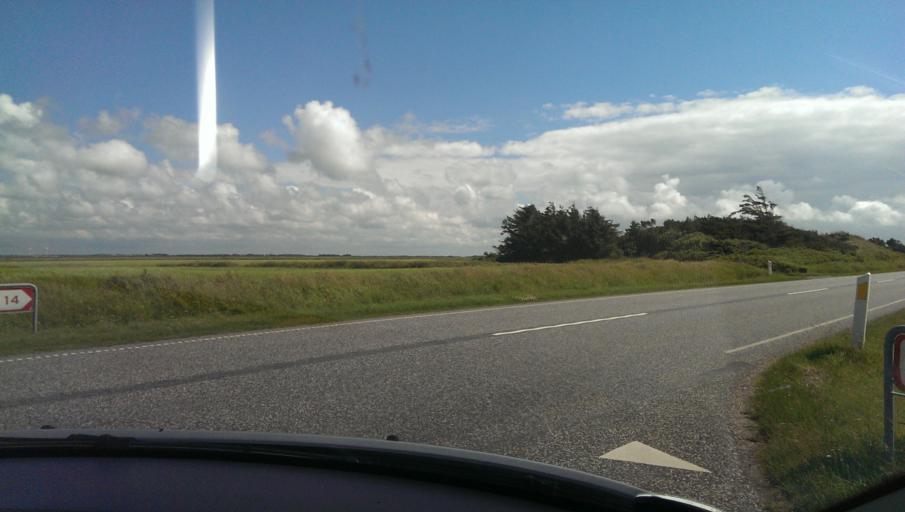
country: DK
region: Central Jutland
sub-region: Holstebro Kommune
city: Ulfborg
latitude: 56.2438
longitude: 8.1394
